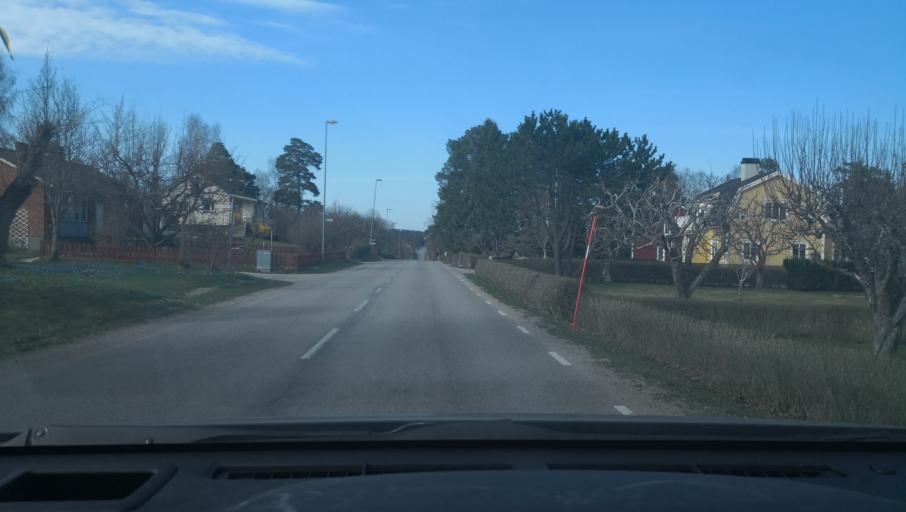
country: SE
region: Uppsala
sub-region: Heby Kommun
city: Heby
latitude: 59.9272
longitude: 16.8555
